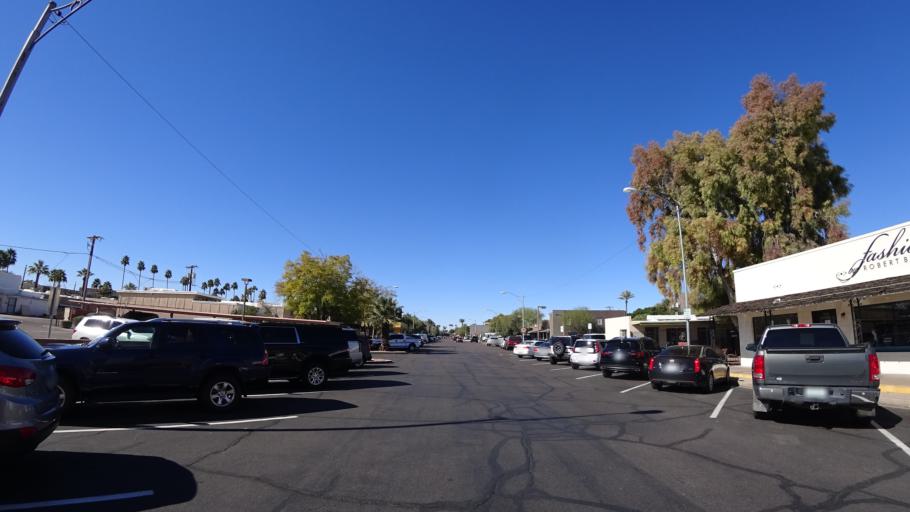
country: US
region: Arizona
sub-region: Maricopa County
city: Scottsdale
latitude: 33.4940
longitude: -111.9268
